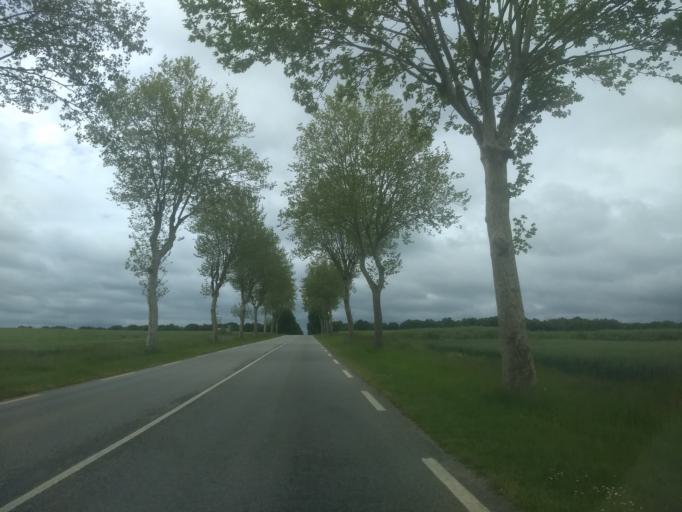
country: FR
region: Centre
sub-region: Departement d'Eure-et-Loir
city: Treon
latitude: 48.6727
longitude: 1.3204
